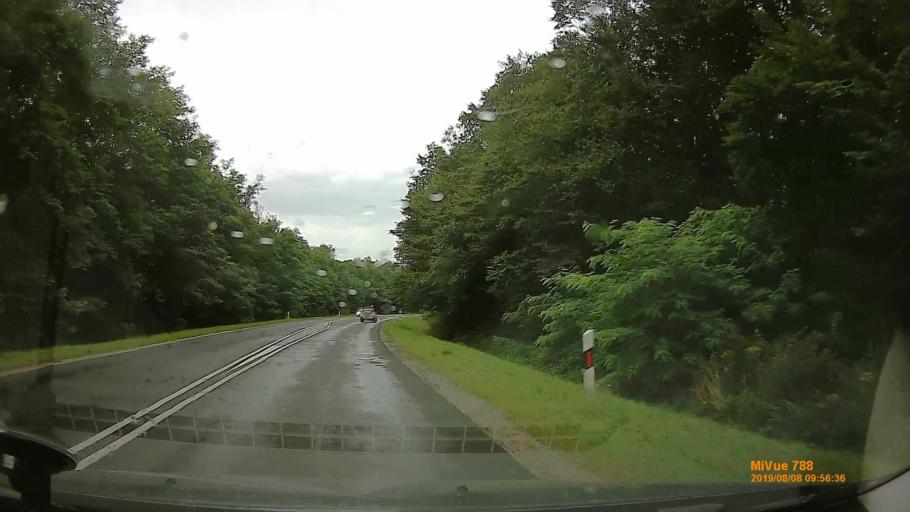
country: HU
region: Vas
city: Vasvar
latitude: 47.0071
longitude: 16.8285
